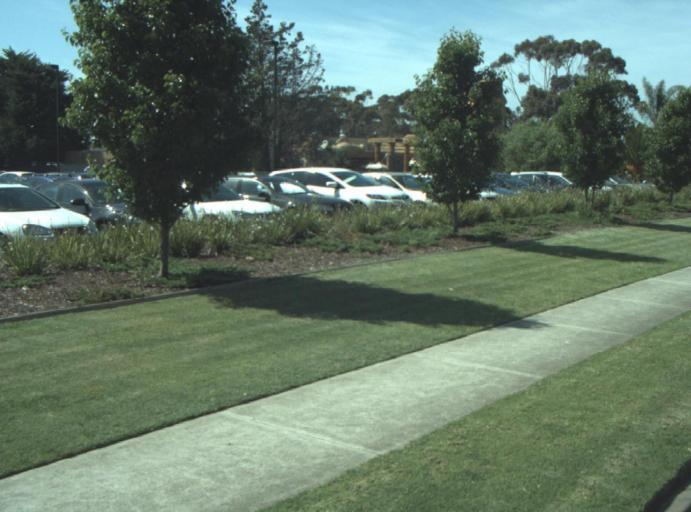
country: AU
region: Victoria
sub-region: Greater Geelong
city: Hamlyn Heights
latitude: -38.1249
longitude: 144.3407
